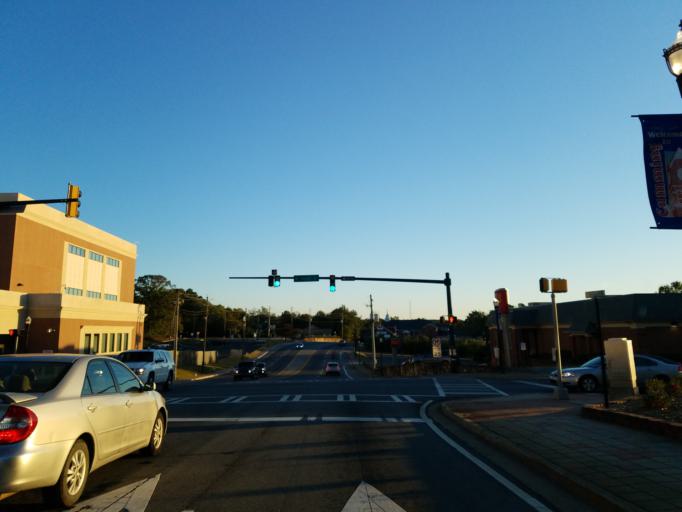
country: US
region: Georgia
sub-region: Forsyth County
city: Cumming
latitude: 34.2063
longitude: -84.1393
